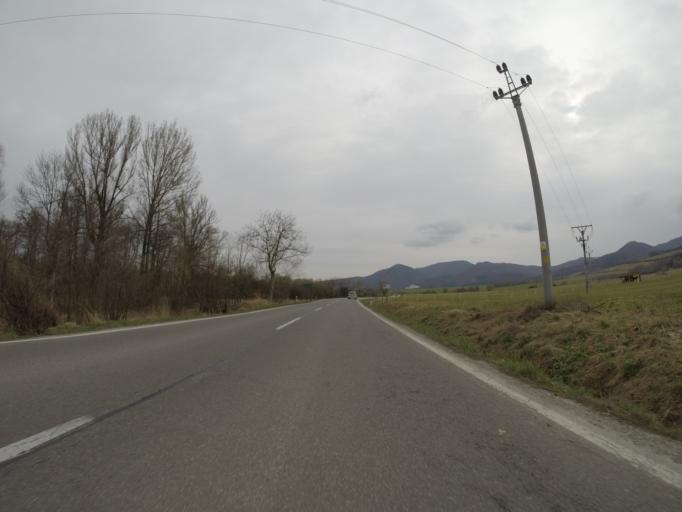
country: SK
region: Nitriansky
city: Bojnice
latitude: 48.8197
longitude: 18.4803
